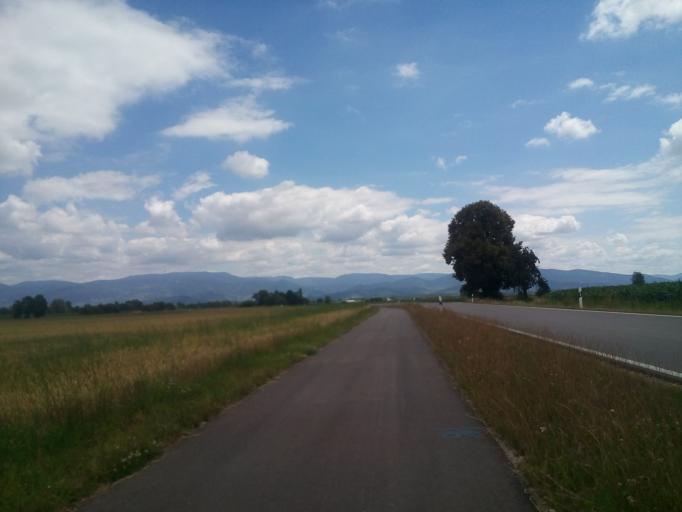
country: DE
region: Baden-Wuerttemberg
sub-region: Freiburg Region
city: Renchen
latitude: 48.6158
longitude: 7.9747
